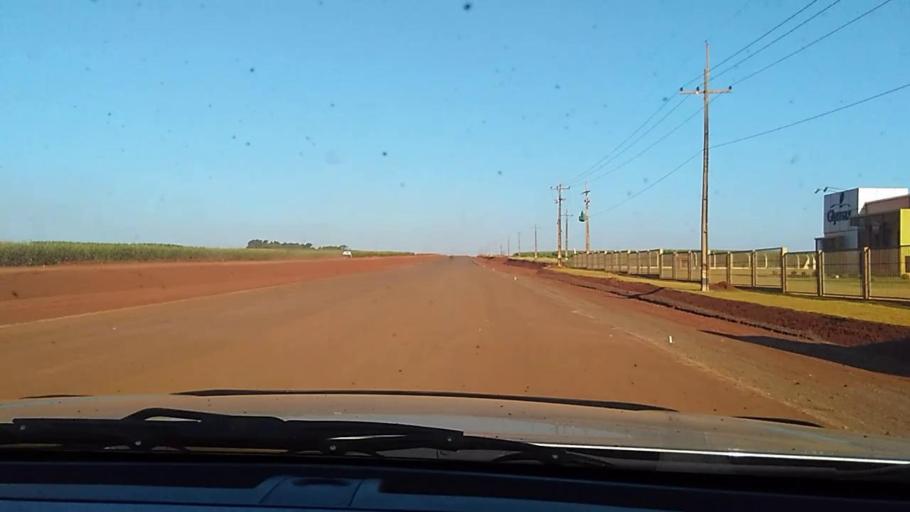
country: PY
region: Alto Parana
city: Naranjal
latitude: -25.9091
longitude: -55.4443
